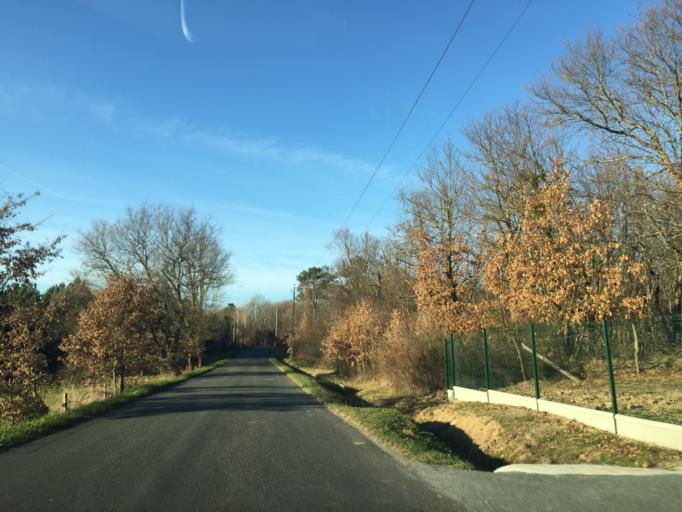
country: FR
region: Aquitaine
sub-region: Departement de la Dordogne
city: Riberac
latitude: 45.2138
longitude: 0.2959
